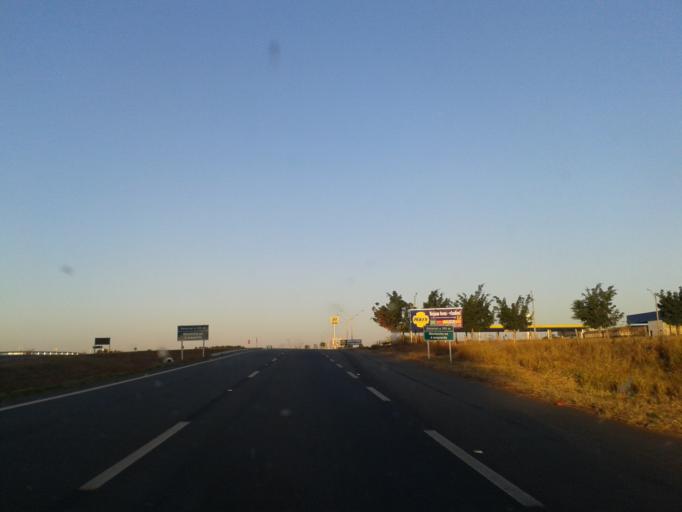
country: BR
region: Goias
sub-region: Itaberai
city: Itaberai
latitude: -16.0192
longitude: -49.8551
